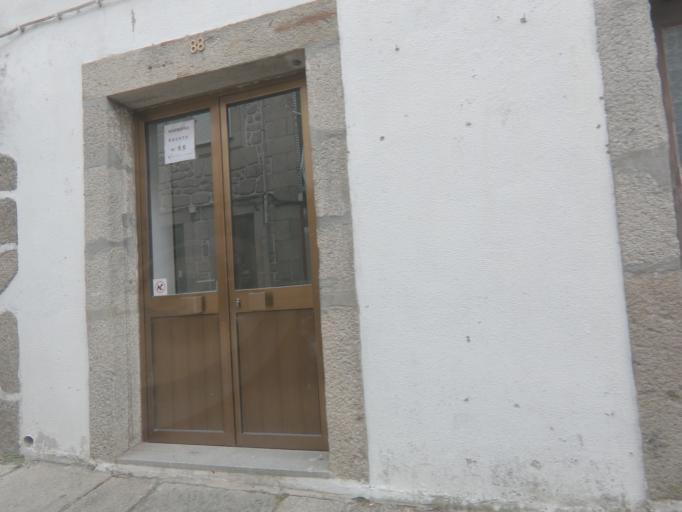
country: PT
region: Viana do Castelo
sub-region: Vila Nova de Cerveira
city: Vila Nova de Cerveira
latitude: 41.9414
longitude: -8.7420
